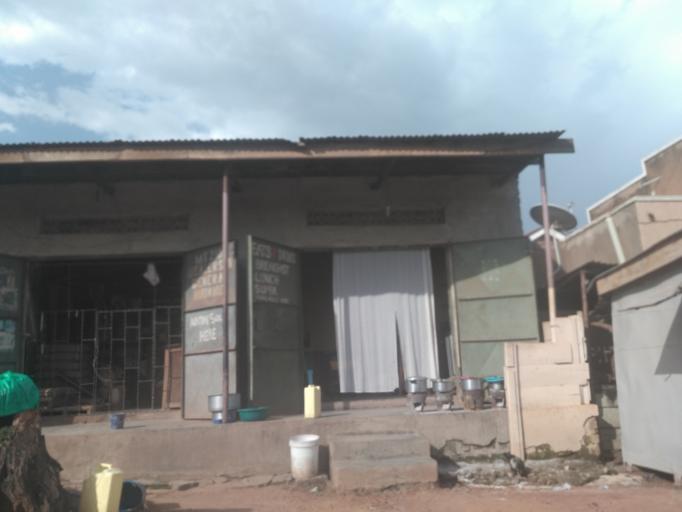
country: UG
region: Central Region
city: Kampala Central Division
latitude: 0.3570
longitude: 32.5821
